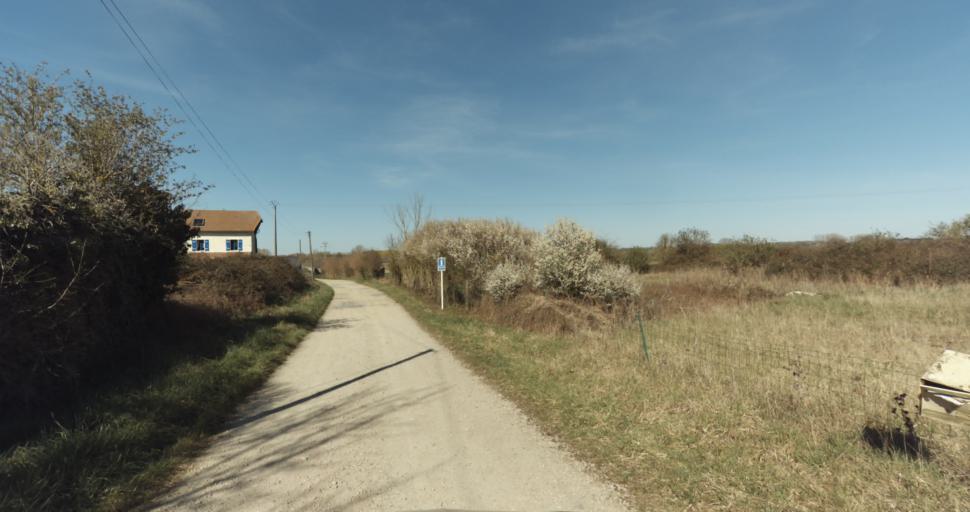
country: FR
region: Lower Normandy
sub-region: Departement du Calvados
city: Saint-Pierre-sur-Dives
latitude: 49.0407
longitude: -0.0207
